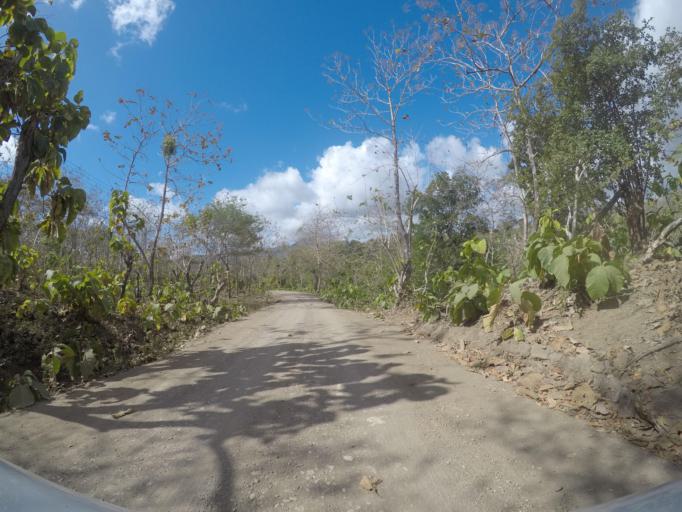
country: TL
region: Lautem
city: Lospalos
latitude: -8.5259
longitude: 126.8414
